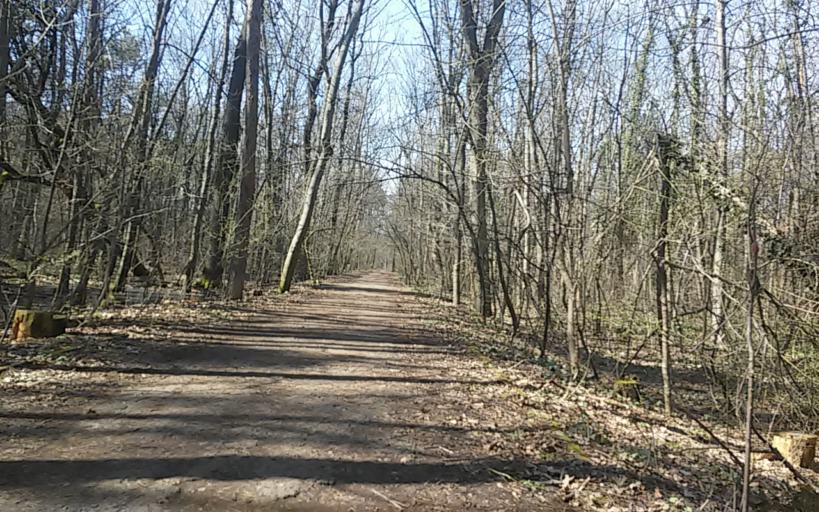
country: BG
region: Sofia-Capital
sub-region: Stolichna Obshtina
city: Sofia
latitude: 42.6802
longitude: 23.3487
